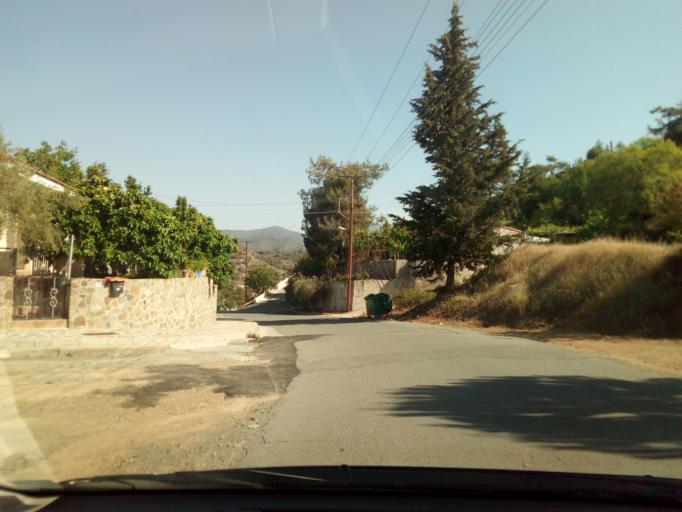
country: CY
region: Limassol
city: Pelendri
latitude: 34.8320
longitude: 33.0389
